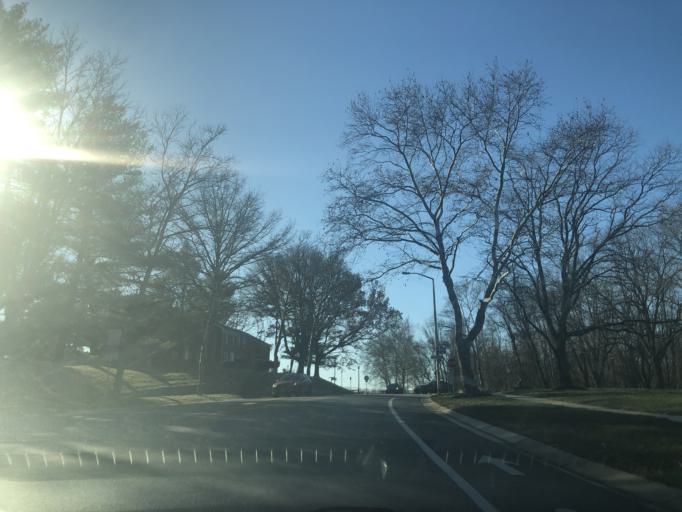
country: US
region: Maryland
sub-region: Howard County
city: Columbia
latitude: 39.2122
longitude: -76.8416
